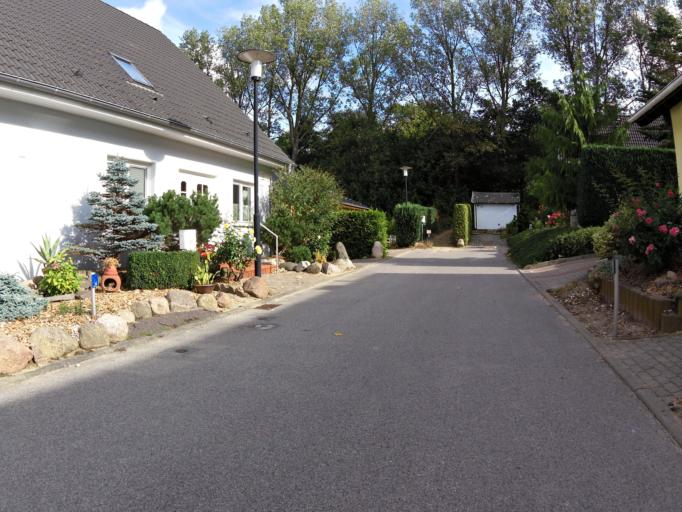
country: DE
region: Mecklenburg-Vorpommern
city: Seebad Bansin
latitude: 53.9648
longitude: 14.1263
